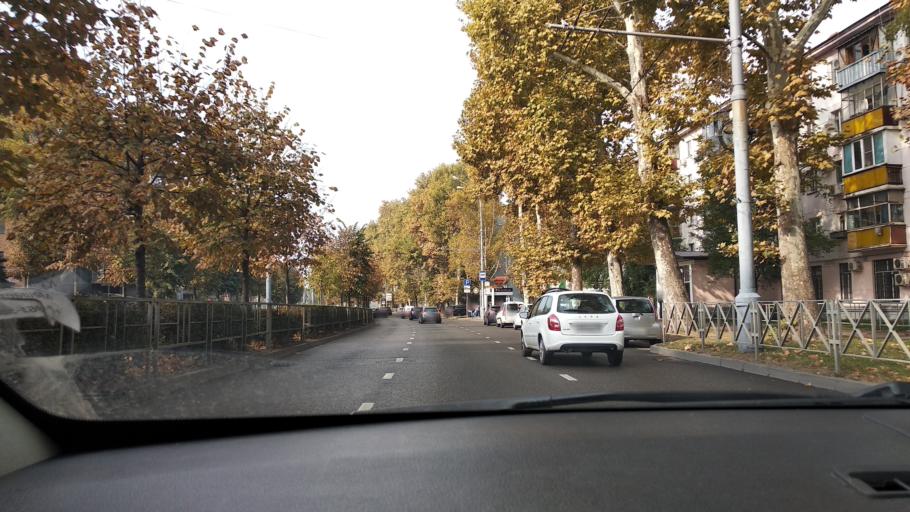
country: RU
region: Krasnodarskiy
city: Krasnodar
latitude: 45.0215
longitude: 39.0189
